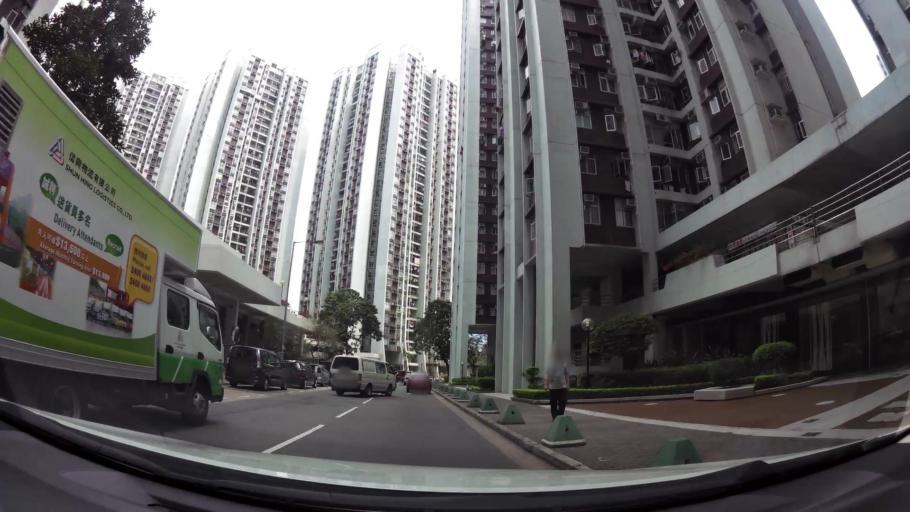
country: HK
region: Wanchai
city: Wan Chai
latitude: 22.2864
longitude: 114.2152
